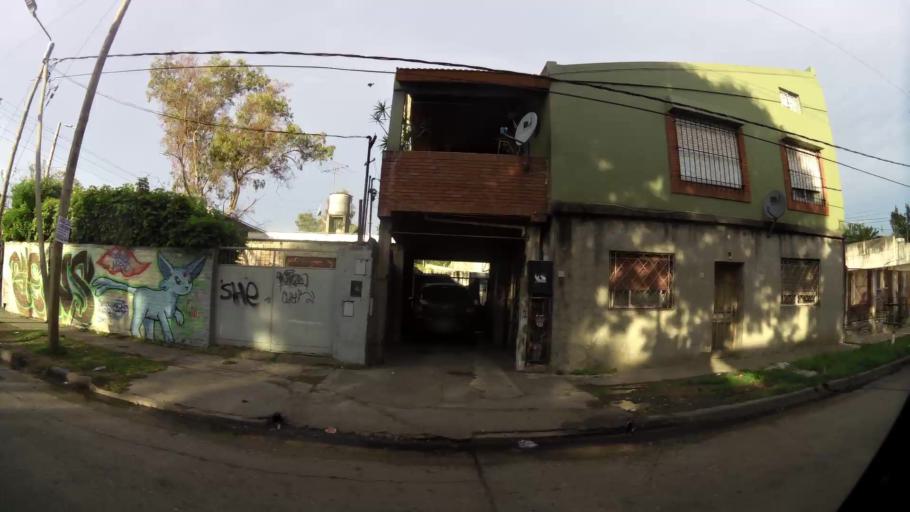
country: AR
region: Buenos Aires
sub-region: Partido de Lomas de Zamora
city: Lomas de Zamora
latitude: -34.7453
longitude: -58.3552
